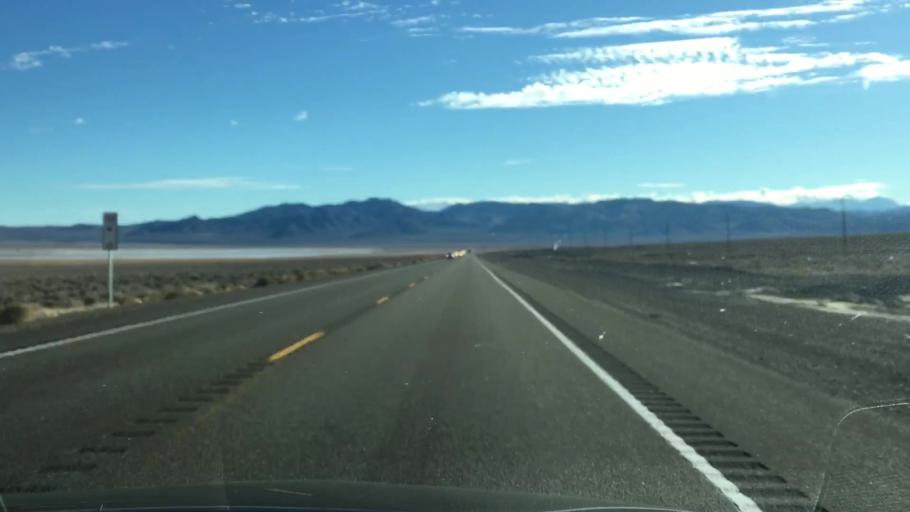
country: US
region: Nevada
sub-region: Mineral County
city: Hawthorne
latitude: 38.3220
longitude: -118.1028
